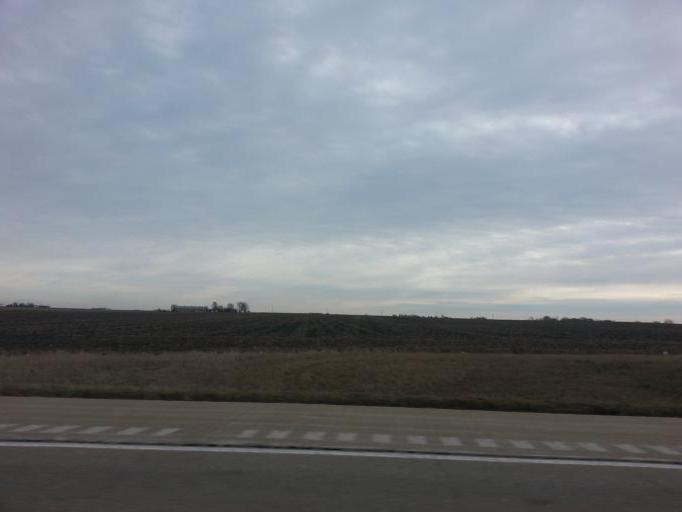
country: US
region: Illinois
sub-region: Woodford County
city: El Paso
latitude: 40.7691
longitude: -89.0346
